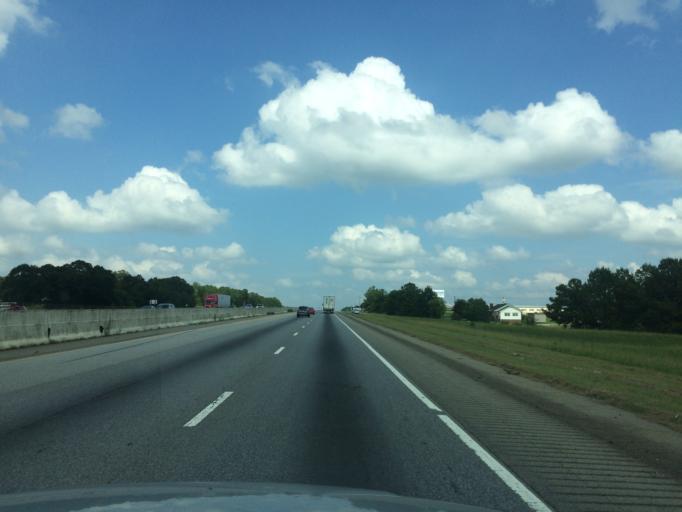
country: US
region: South Carolina
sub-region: Spartanburg County
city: Mayo
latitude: 35.0267
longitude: -81.8755
